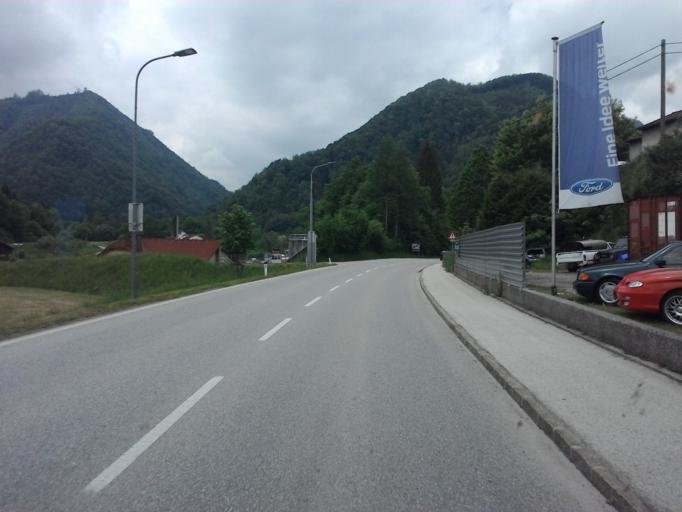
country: AT
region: Upper Austria
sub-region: Politischer Bezirk Steyr-Land
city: Maria Neustift
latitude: 47.8834
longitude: 14.5425
